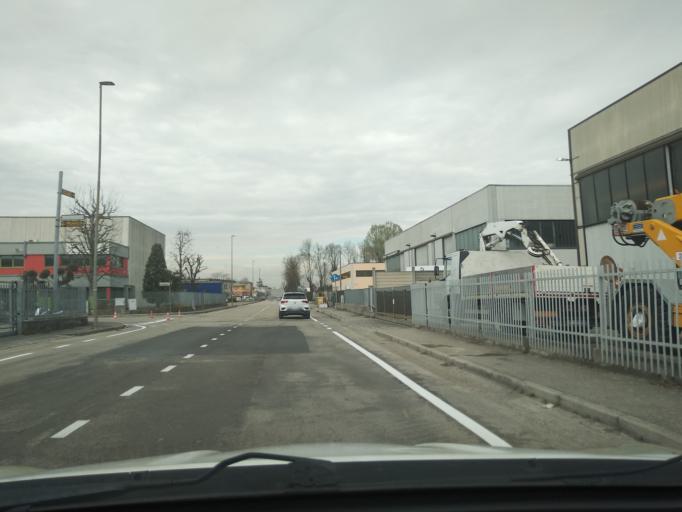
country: IT
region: Veneto
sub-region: Provincia di Padova
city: Rubano
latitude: 45.4214
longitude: 11.7924
